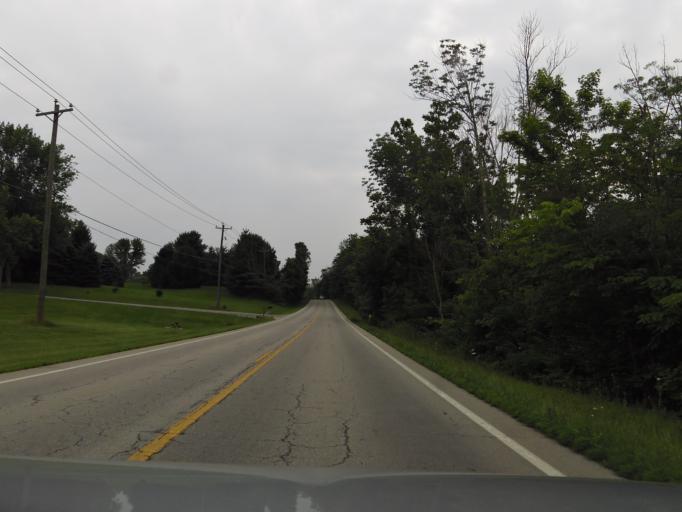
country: US
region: Ohio
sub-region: Clinton County
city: Blanchester
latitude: 39.2533
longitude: -83.9040
